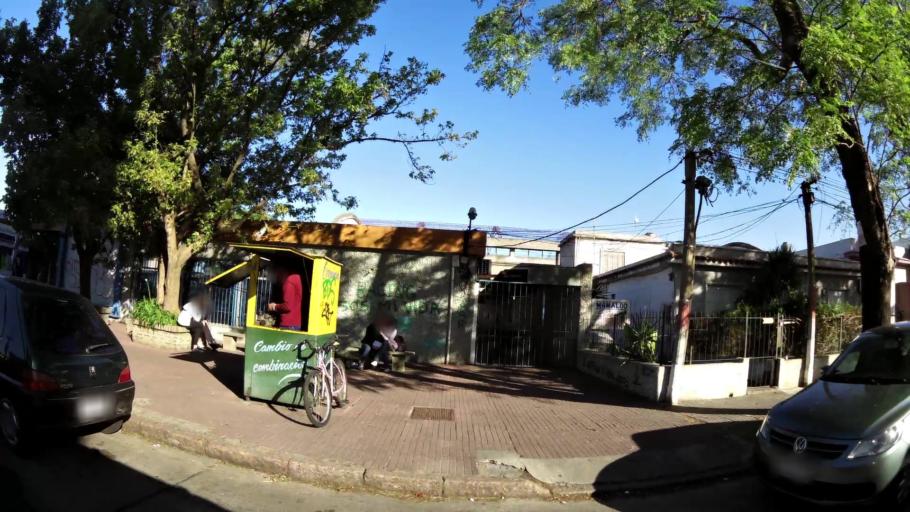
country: UY
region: Canelones
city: La Paz
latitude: -34.8341
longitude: -56.2162
